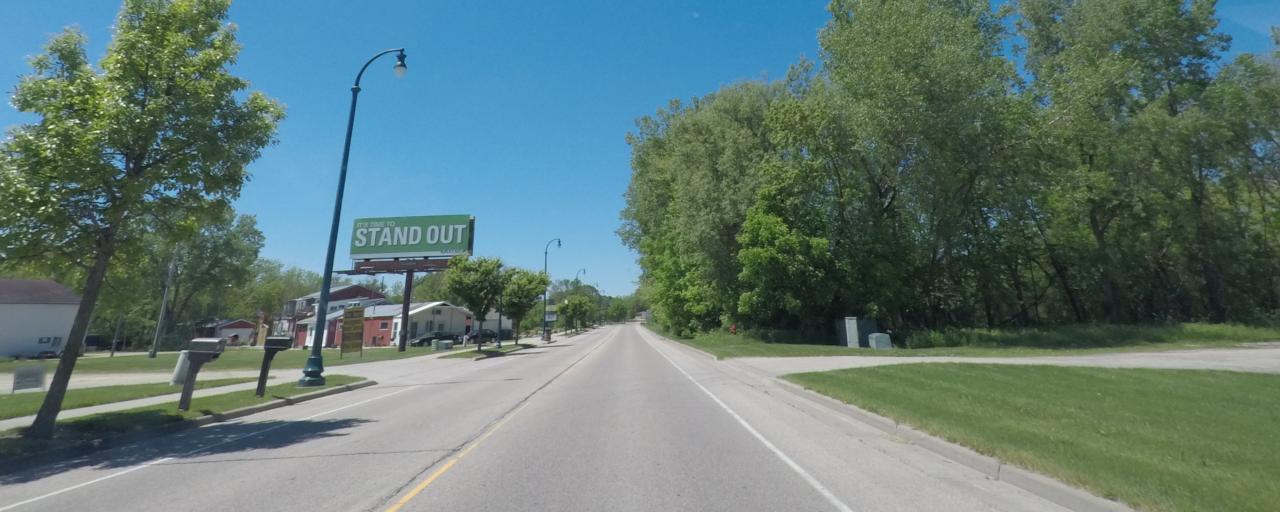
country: US
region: Wisconsin
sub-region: Rock County
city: Evansville
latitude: 42.7828
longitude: -89.2955
